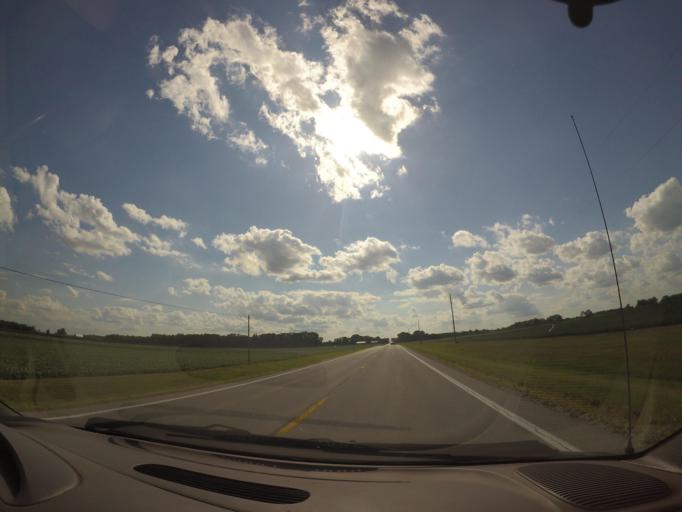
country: US
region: Ohio
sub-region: Sandusky County
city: Gibsonburg
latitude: 41.3413
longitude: -83.3985
